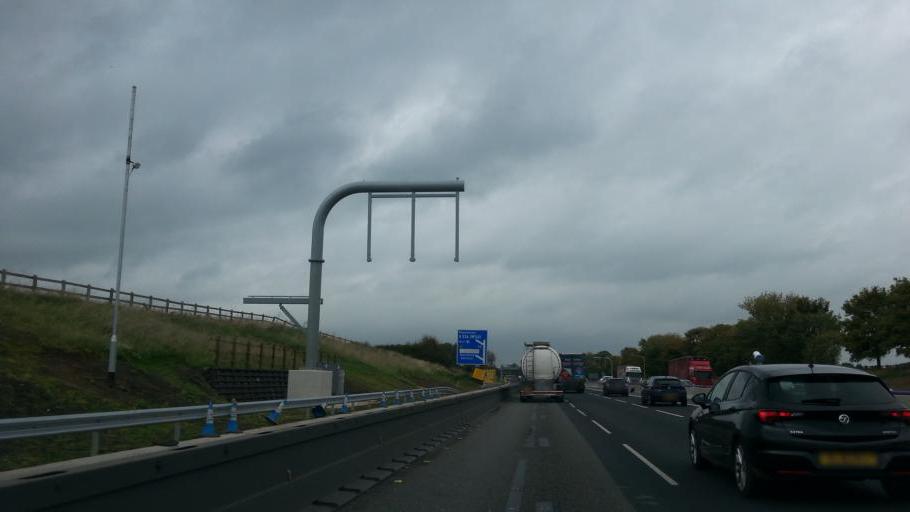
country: GB
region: England
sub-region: Cheshire East
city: Knutsford
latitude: 53.2926
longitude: -2.3970
